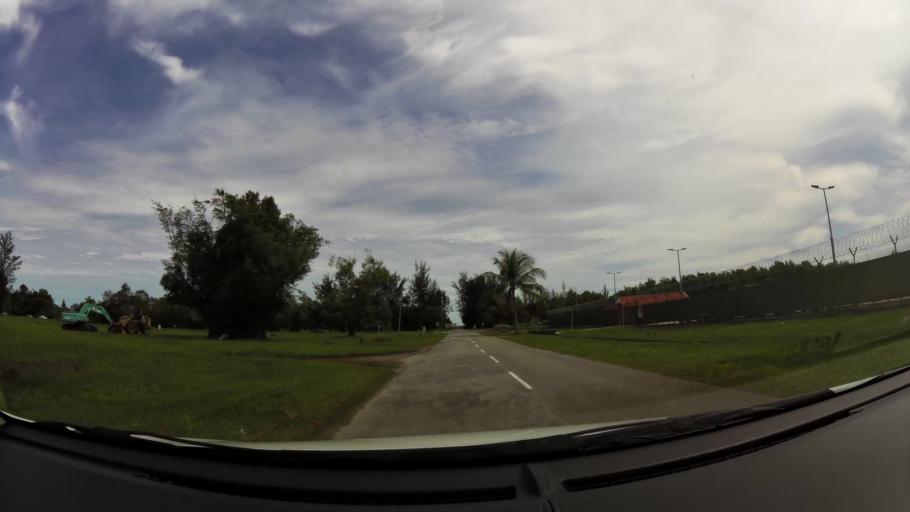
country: BN
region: Belait
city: Seria
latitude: 4.6085
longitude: 114.3118
